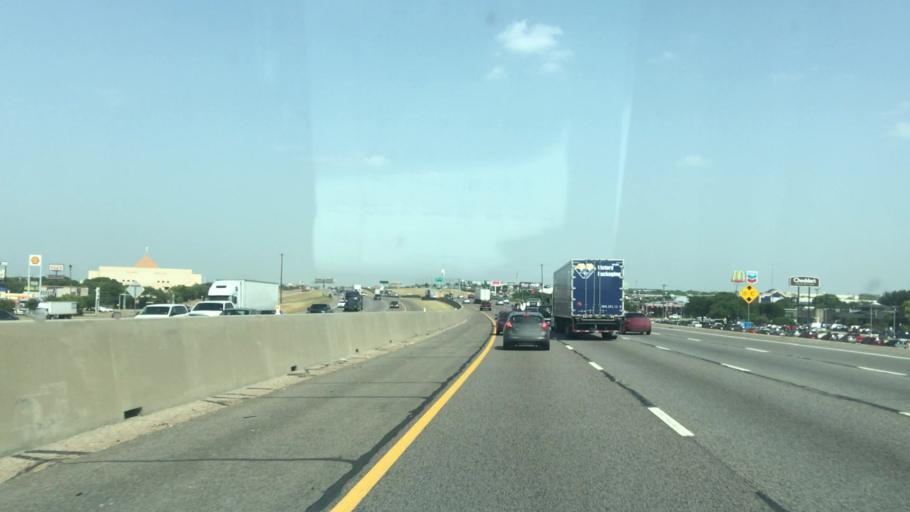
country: US
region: Texas
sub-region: Dallas County
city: Duncanville
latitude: 32.6466
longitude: -96.8604
